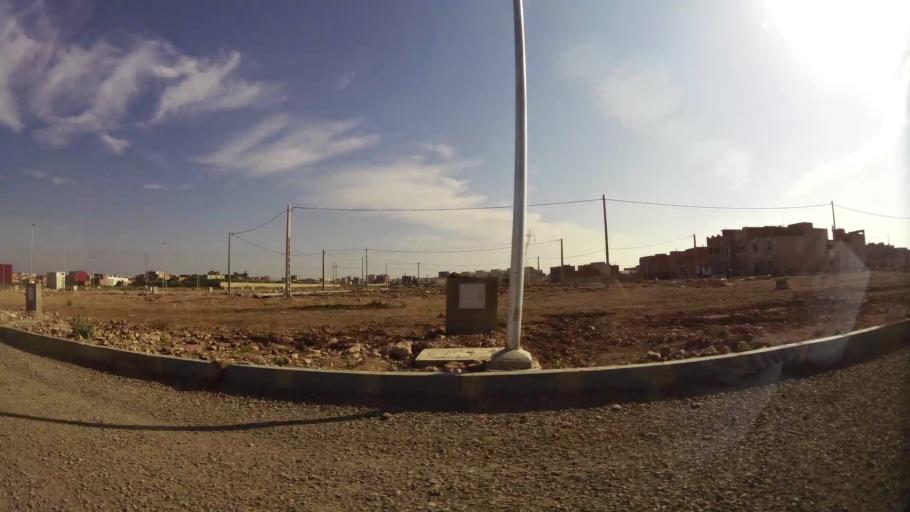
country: MA
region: Oriental
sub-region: Oujda-Angad
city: Oujda
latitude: 34.7248
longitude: -1.8860
